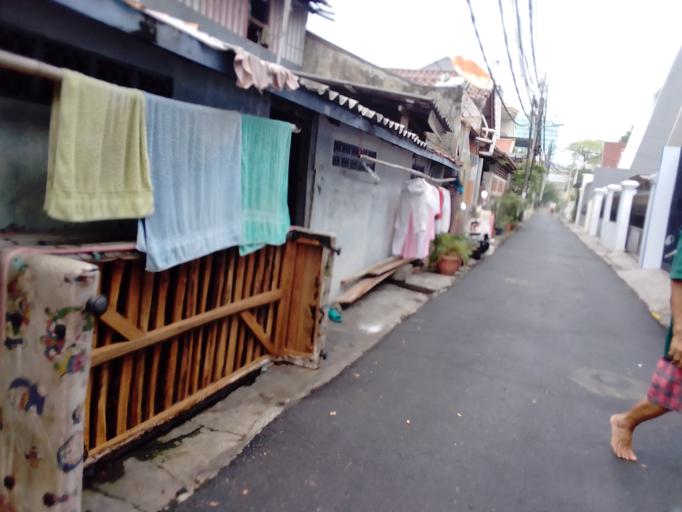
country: ID
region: Jakarta Raya
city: Jakarta
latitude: -6.1671
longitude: 106.8097
